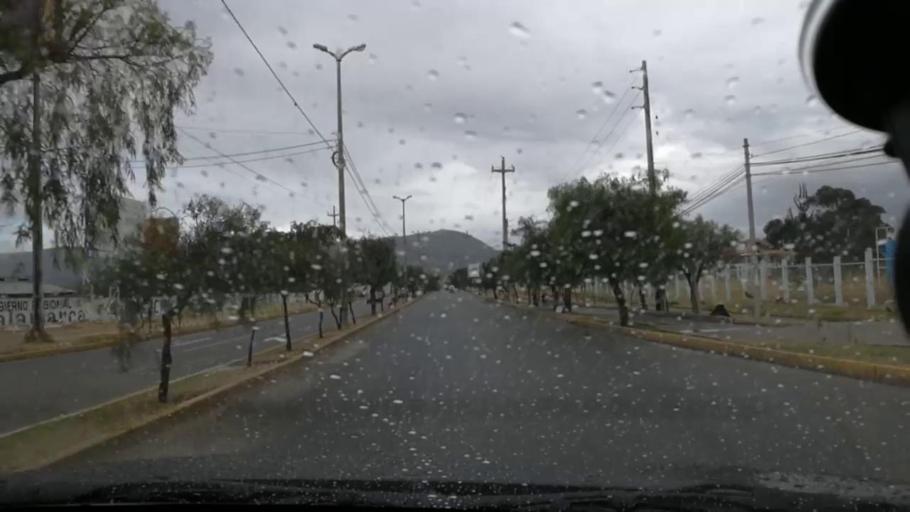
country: PE
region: Cajamarca
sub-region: Provincia de Cajamarca
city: Cajamarca
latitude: -7.1654
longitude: -78.4940
